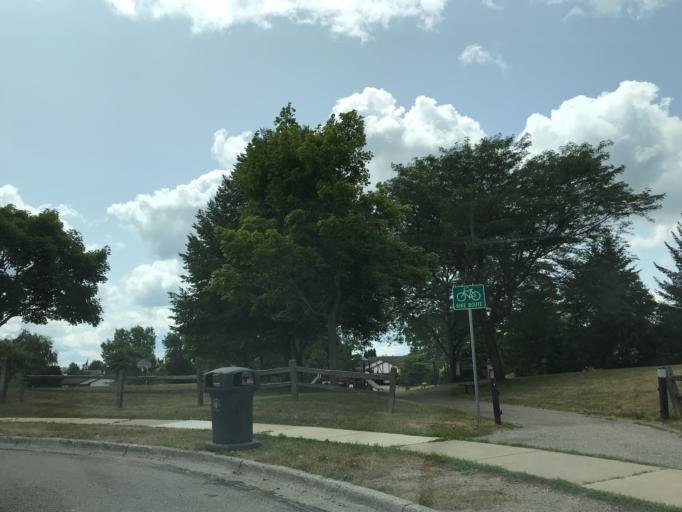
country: US
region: Michigan
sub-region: Washtenaw County
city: Ann Arbor
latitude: 42.2506
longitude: -83.7638
